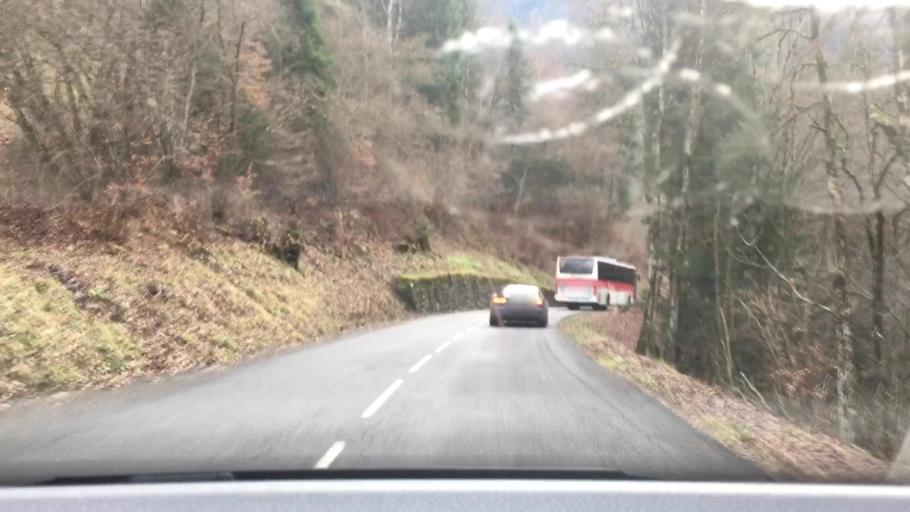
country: FR
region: Rhone-Alpes
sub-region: Departement de la Haute-Savoie
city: Abondance
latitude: 46.2556
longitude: 6.6310
